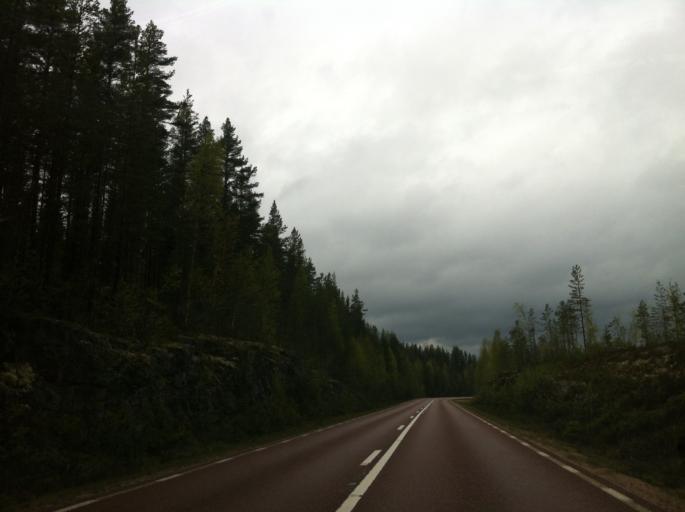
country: SE
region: Jaemtland
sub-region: Harjedalens Kommun
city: Sveg
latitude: 61.8892
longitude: 14.6238
